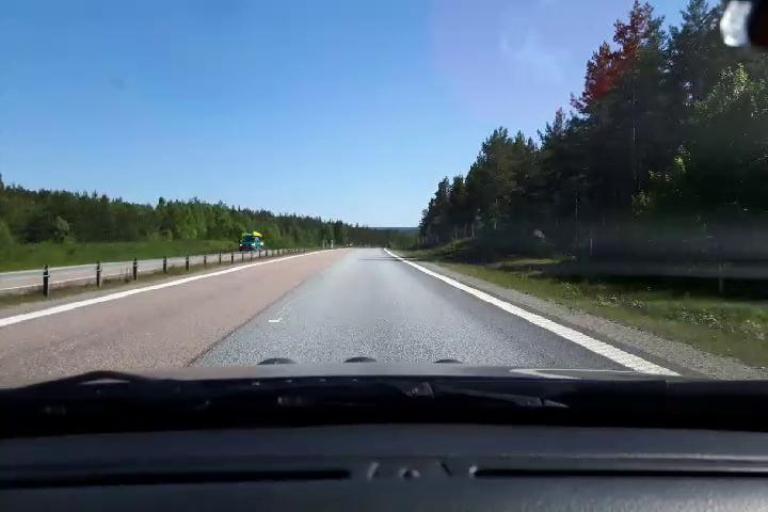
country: SE
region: Gaevleborg
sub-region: Soderhamns Kommun
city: Soderhamn
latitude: 61.3683
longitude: 17.0083
